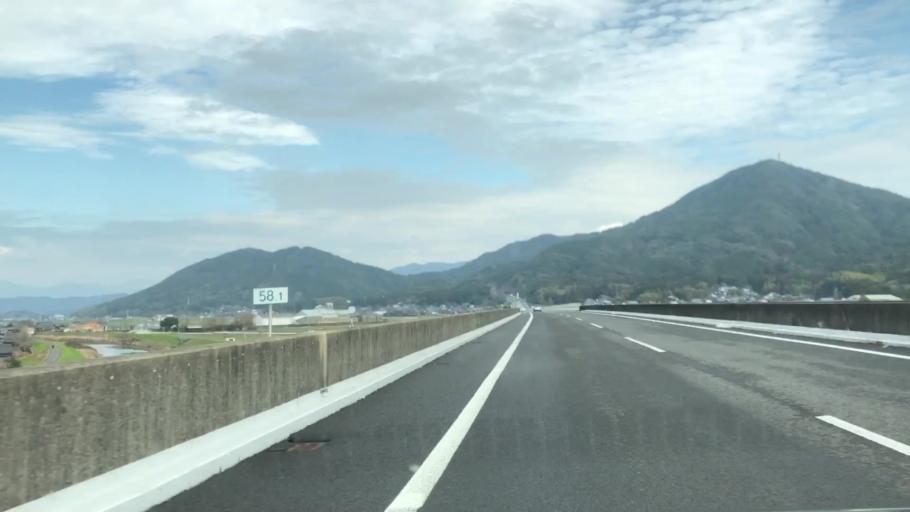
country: JP
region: Saga Prefecture
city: Takeocho-takeo
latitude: 33.1791
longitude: 130.0481
